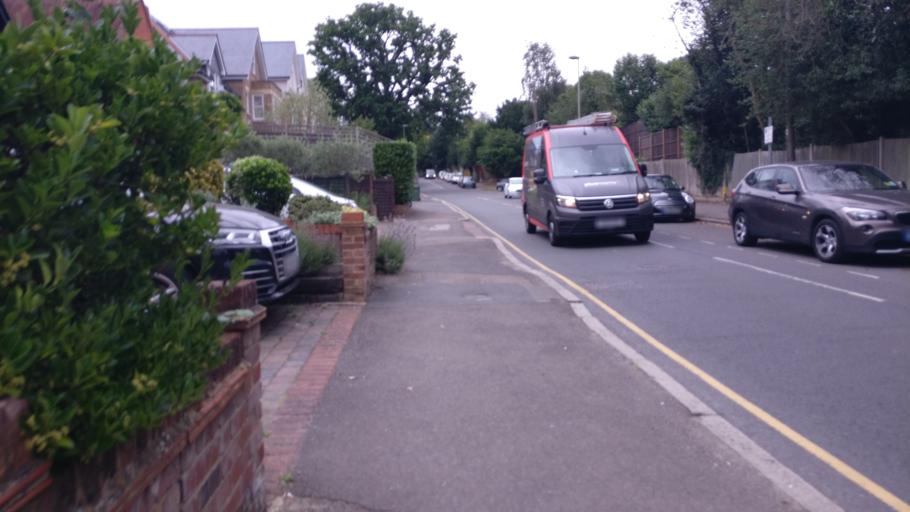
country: GB
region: England
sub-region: Surrey
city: Weybridge
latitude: 51.3719
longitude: -0.4550
